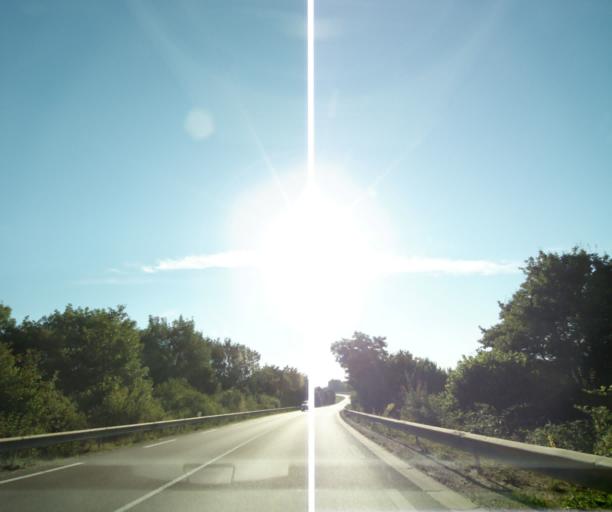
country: FR
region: Ile-de-France
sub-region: Departement de Seine-et-Marne
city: Saint-Germain-Laval
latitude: 48.3823
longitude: 3.0039
